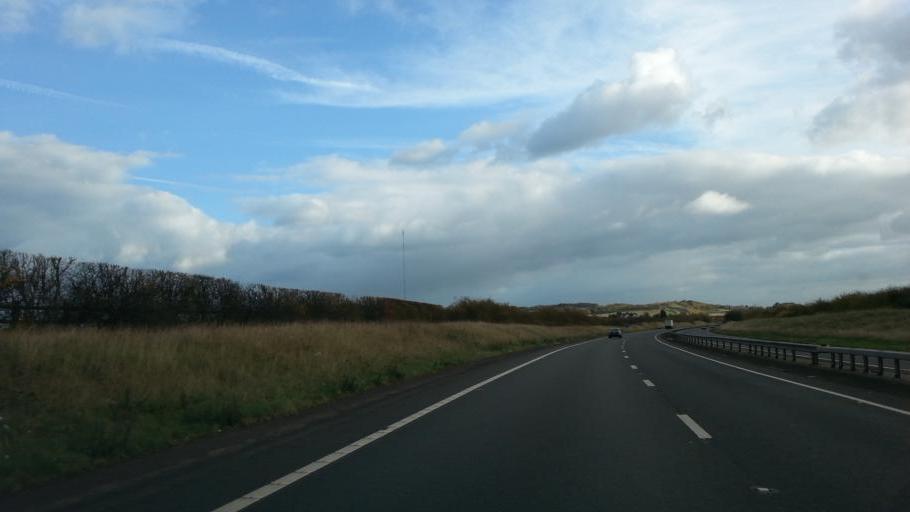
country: GB
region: England
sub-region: Staffordshire
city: Shenstone
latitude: 52.6398
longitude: -1.7989
